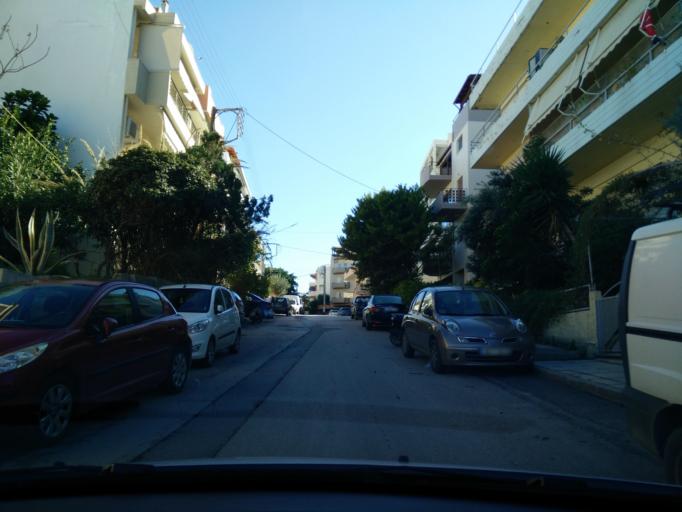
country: GR
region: Crete
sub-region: Nomos Irakleiou
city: Irakleion
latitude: 35.3293
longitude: 25.1416
